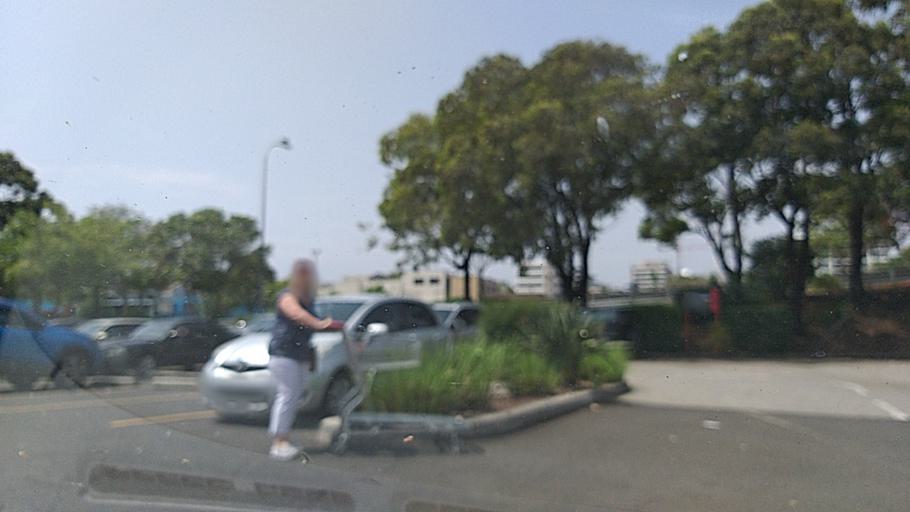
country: AU
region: New South Wales
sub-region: Wollongong
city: Gwynneville
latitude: -34.4187
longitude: 150.8913
